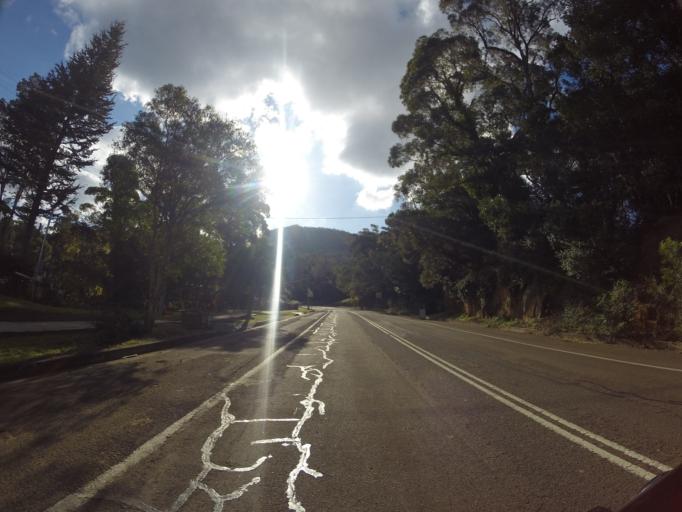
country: AU
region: New South Wales
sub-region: Wollongong
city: Mount Keira
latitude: -34.4118
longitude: 150.8582
